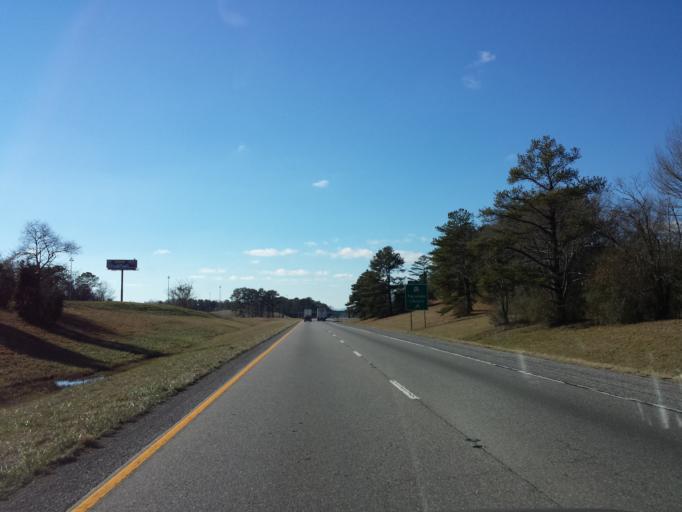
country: US
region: Alabama
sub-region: Talladega County
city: Lincoln
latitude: 33.5909
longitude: -86.1172
